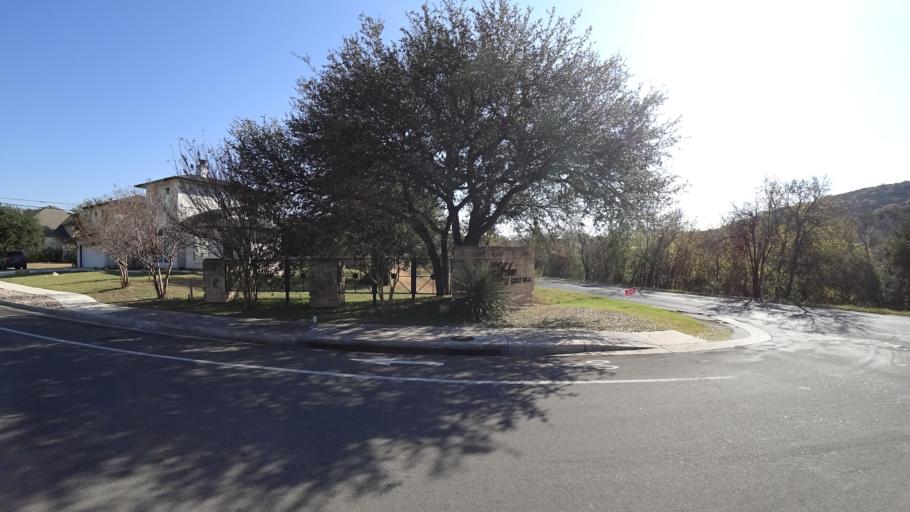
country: US
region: Texas
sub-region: Williamson County
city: Jollyville
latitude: 30.3912
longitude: -97.7768
